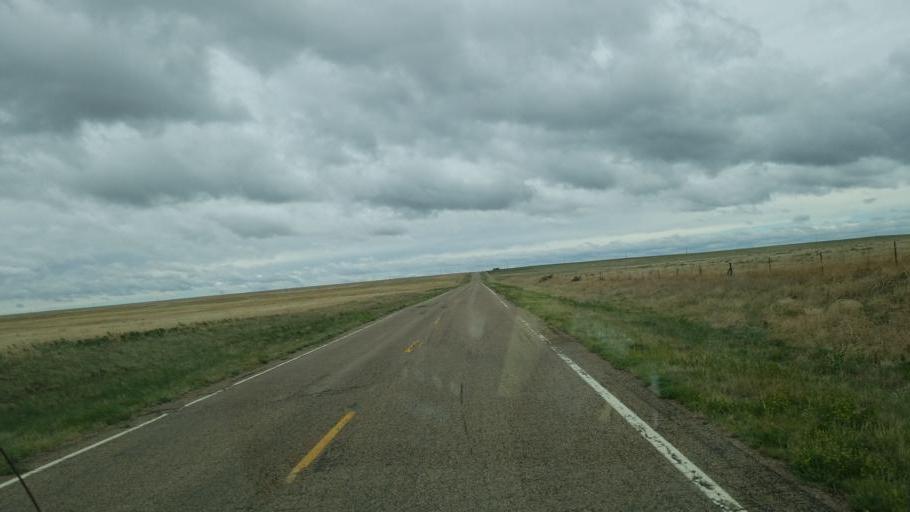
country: US
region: Colorado
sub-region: Lincoln County
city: Hugo
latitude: 38.8510
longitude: -103.6152
